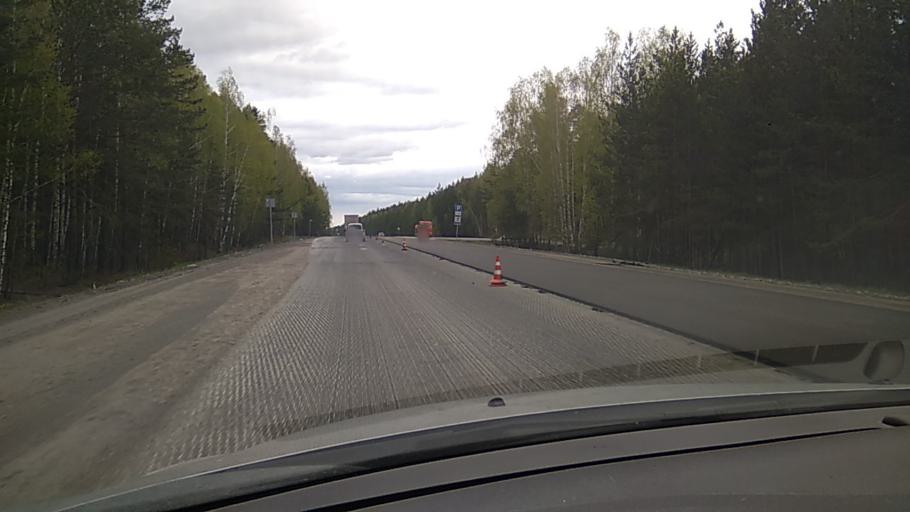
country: RU
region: Sverdlovsk
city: Verkhneye Dubrovo
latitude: 56.6901
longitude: 61.1070
